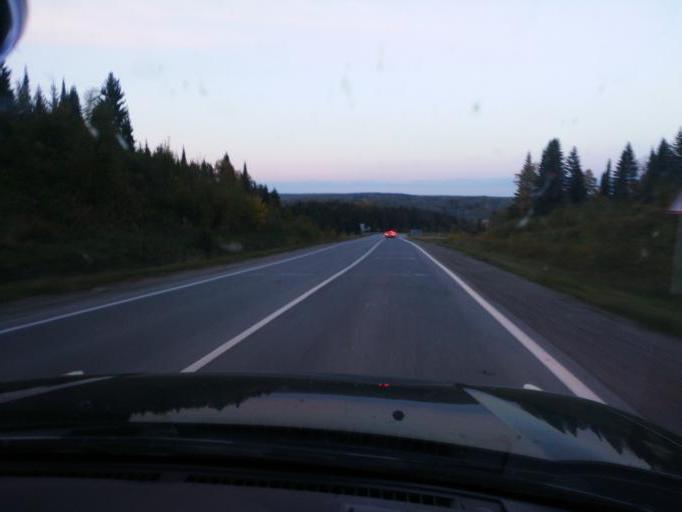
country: RU
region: Perm
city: Sylva
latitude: 58.2927
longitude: 56.8362
